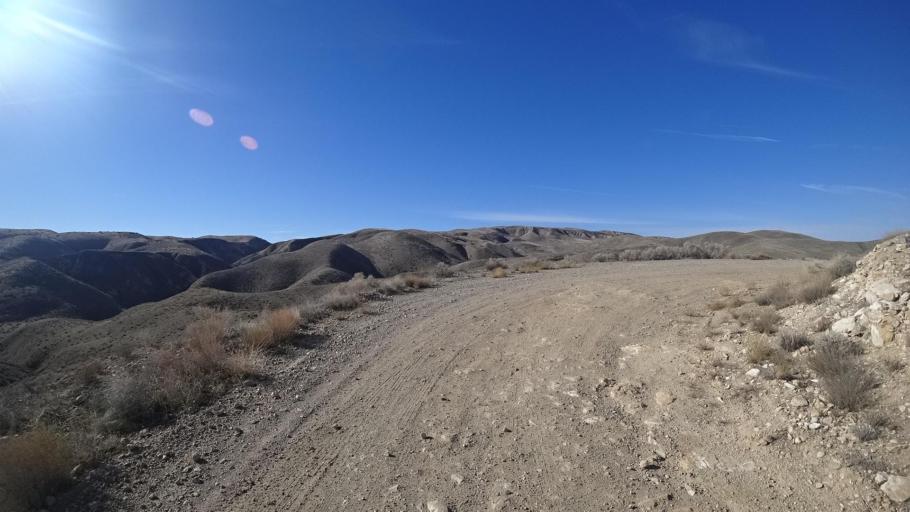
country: US
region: California
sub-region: Kern County
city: Maricopa
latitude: 35.0145
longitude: -119.4723
